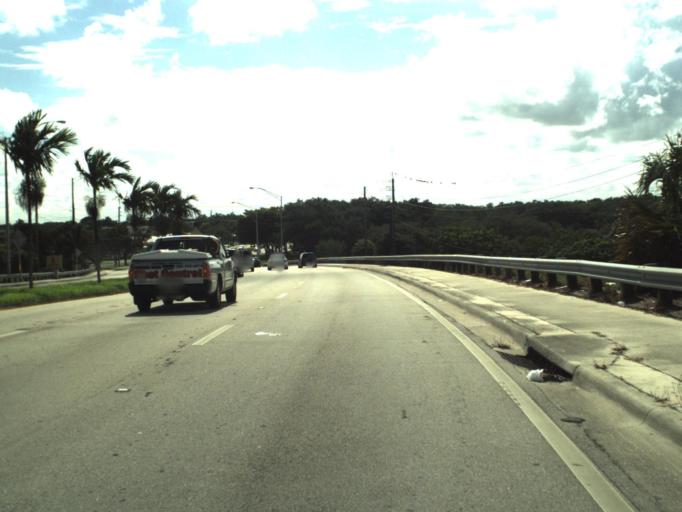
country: US
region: Florida
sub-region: Broward County
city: Hollywood
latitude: 26.0336
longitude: -80.1685
